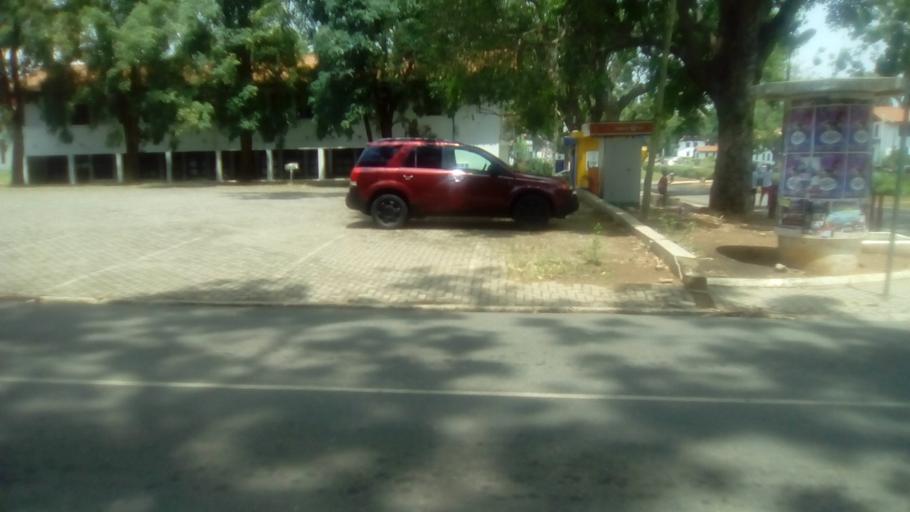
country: GH
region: Greater Accra
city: Medina Estates
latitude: 5.6508
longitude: -0.1891
